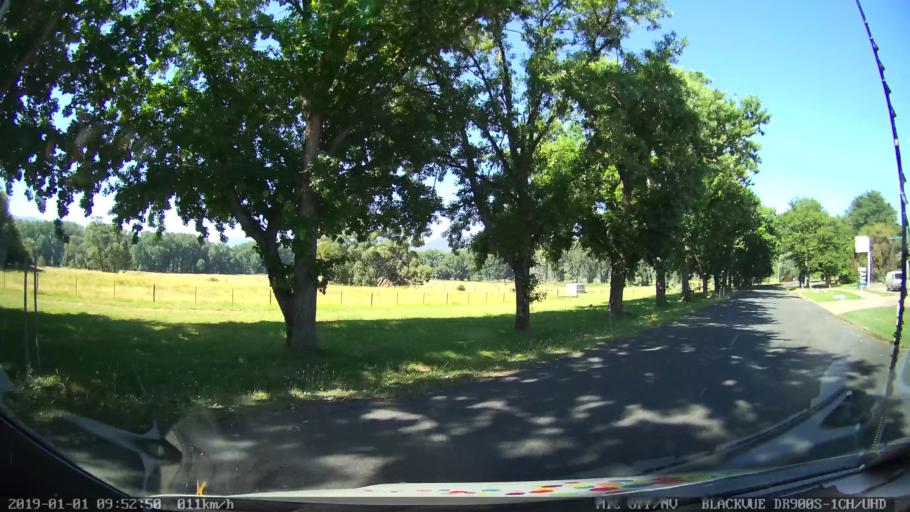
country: AU
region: New South Wales
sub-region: Snowy River
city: Jindabyne
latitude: -36.2196
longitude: 148.1246
